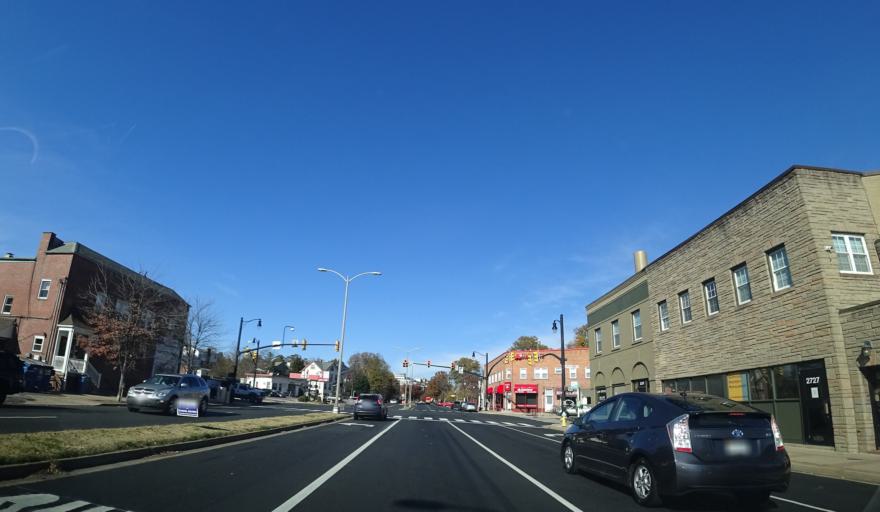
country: US
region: Virginia
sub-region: Arlington County
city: Arlington
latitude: 38.8804
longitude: -77.0902
